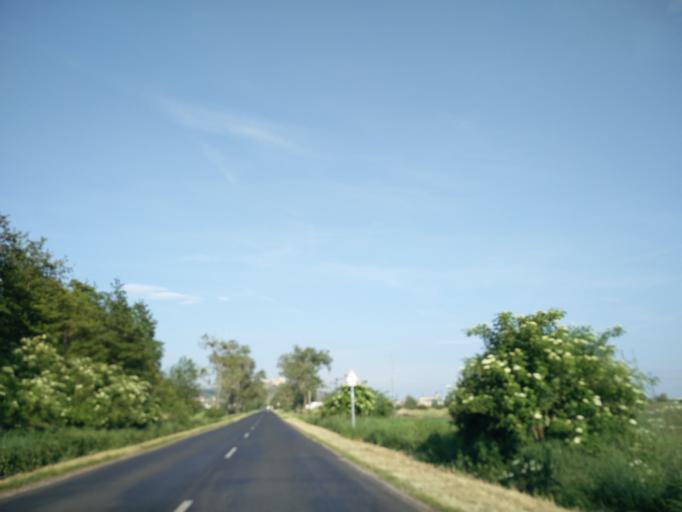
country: HU
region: Veszprem
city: Sumeg
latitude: 46.9841
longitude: 17.2573
